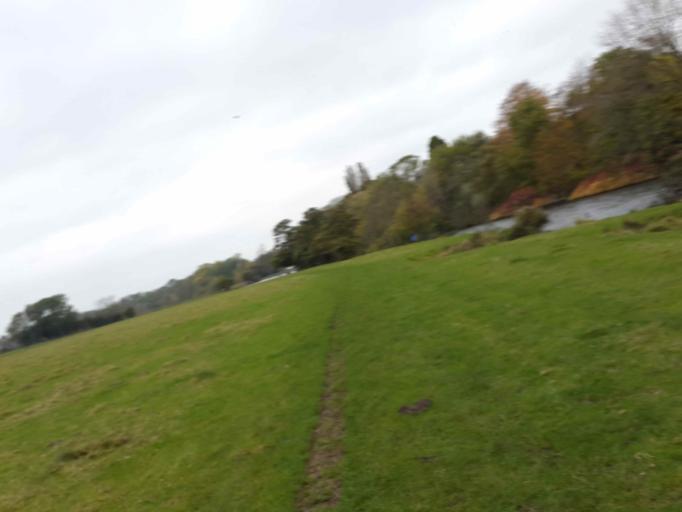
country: GB
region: England
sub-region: Oxfordshire
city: Radley
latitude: 51.6577
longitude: -1.1890
